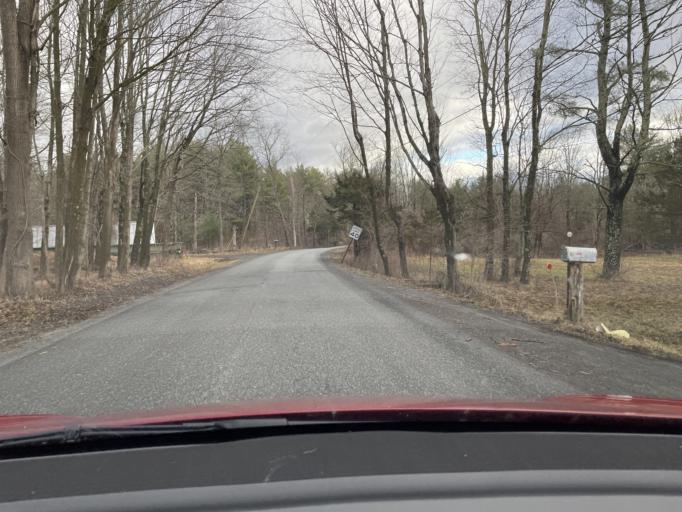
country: US
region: New York
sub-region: Ulster County
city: Manorville
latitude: 42.0776
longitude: -74.0409
